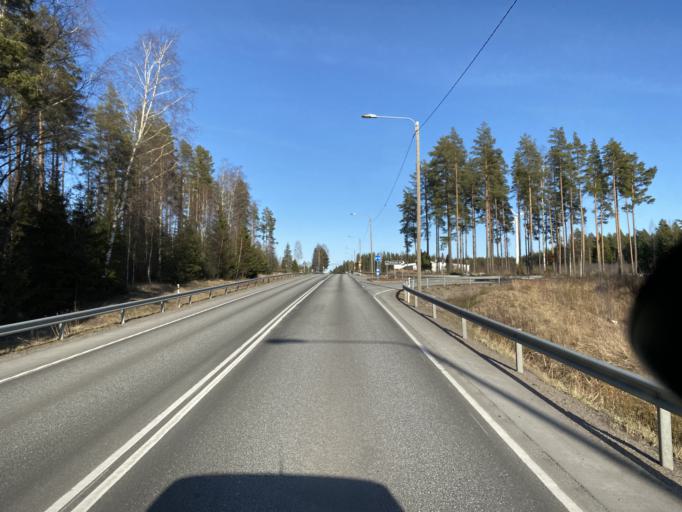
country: FI
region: Satakunta
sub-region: Rauma
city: Eura
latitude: 61.1463
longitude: 22.2167
